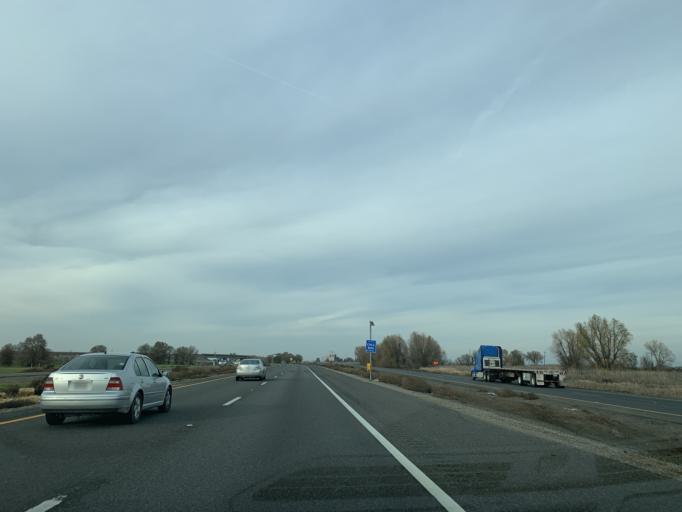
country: US
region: California
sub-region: Sacramento County
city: Elverta
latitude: 38.8477
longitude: -121.5435
